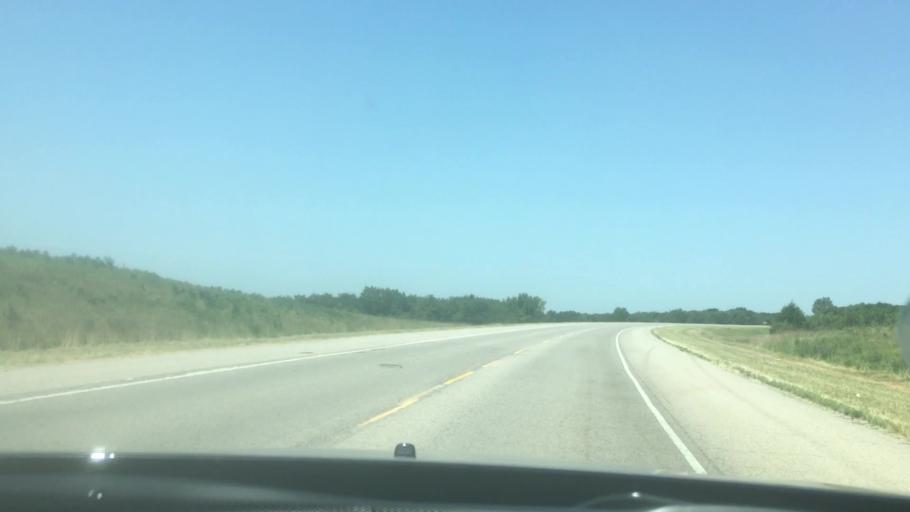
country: US
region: Oklahoma
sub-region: Pontotoc County
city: Ada
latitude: 34.6423
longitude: -96.5375
